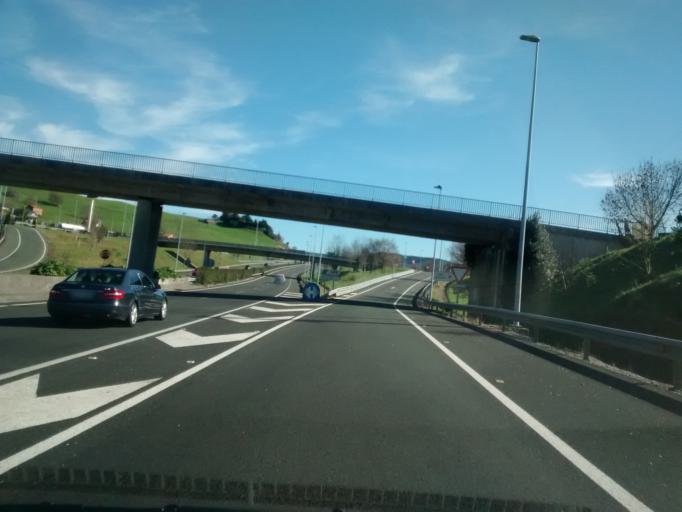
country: ES
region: Cantabria
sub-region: Provincia de Cantabria
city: Entrambasaguas
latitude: 43.3894
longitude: -3.6863
